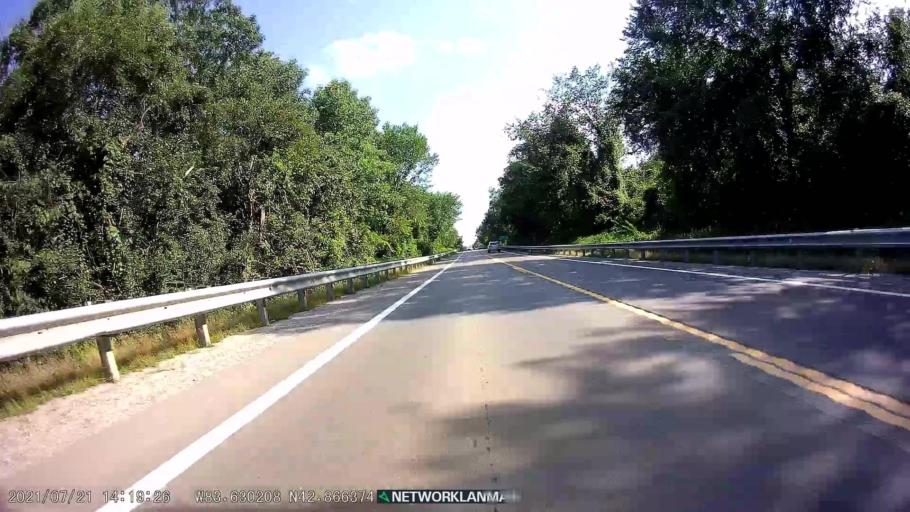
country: US
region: Michigan
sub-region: Genesee County
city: Grand Blanc
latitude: 42.8670
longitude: -83.6302
